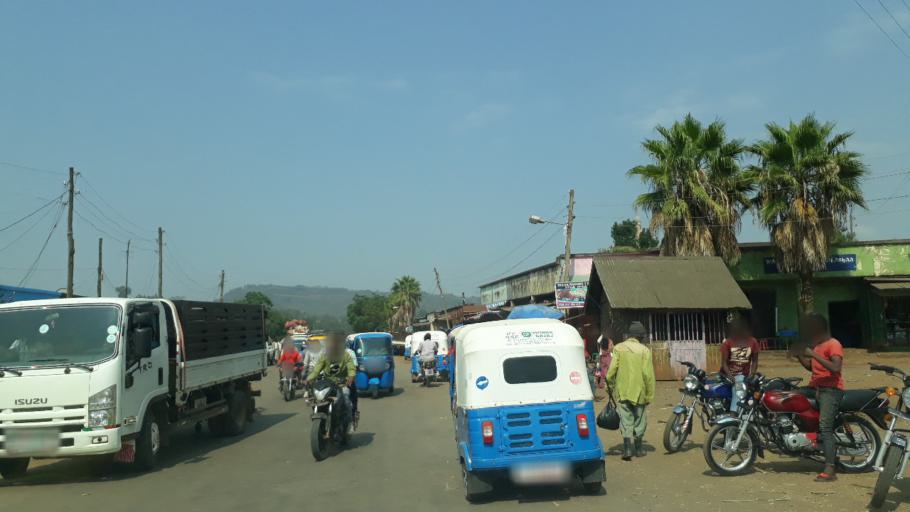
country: ET
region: Oromiya
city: Agaro
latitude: 7.8583
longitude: 36.5815
